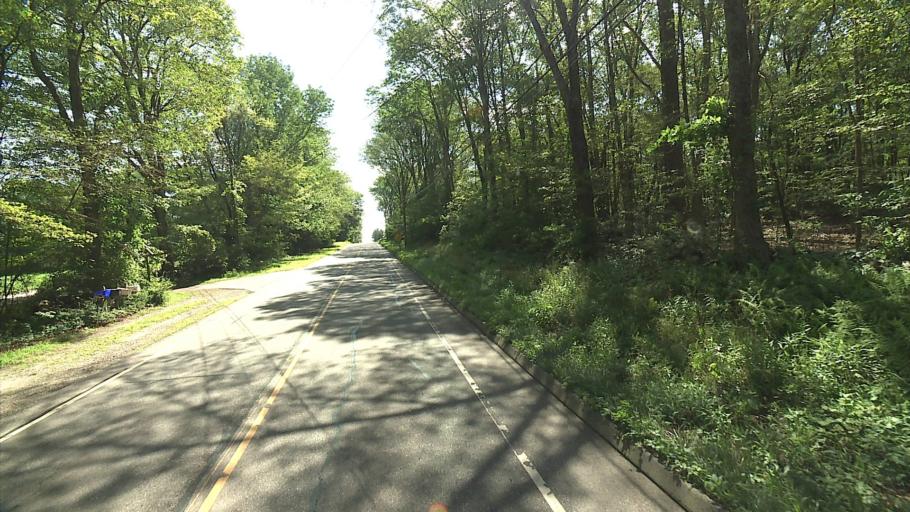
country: US
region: Connecticut
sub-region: Windham County
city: Windham
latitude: 41.6979
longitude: -72.0996
